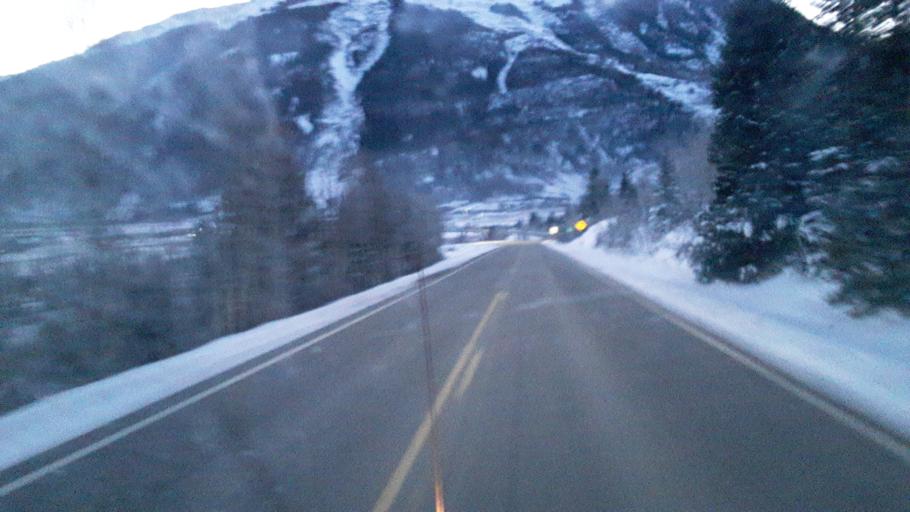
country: US
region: Colorado
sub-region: San Juan County
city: Silverton
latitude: 37.8055
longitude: -107.6778
